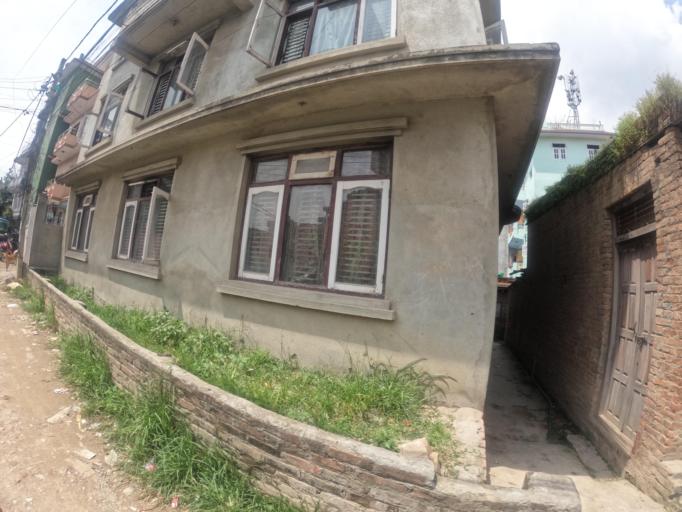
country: NP
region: Central Region
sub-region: Bagmati Zone
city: Bhaktapur
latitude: 27.6750
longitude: 85.3736
